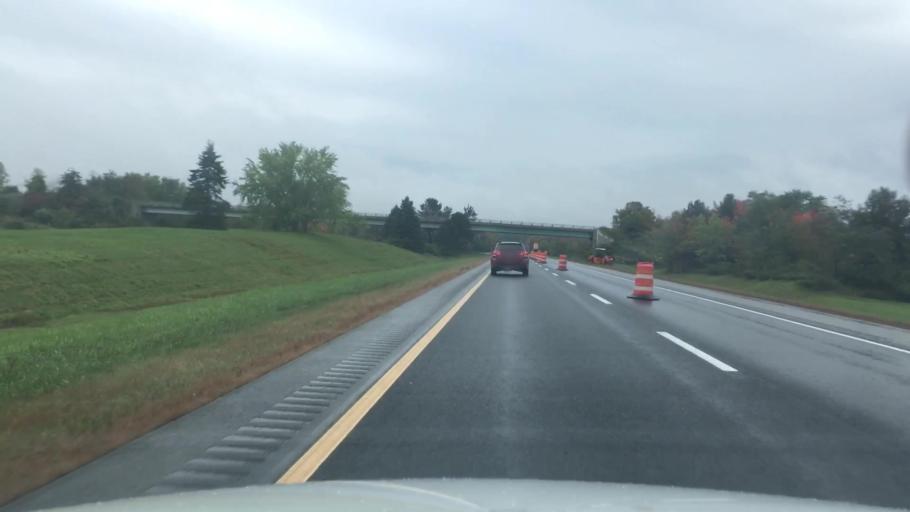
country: US
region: Maine
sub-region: Sagadahoc County
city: Richmond
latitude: 44.1486
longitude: -69.8393
